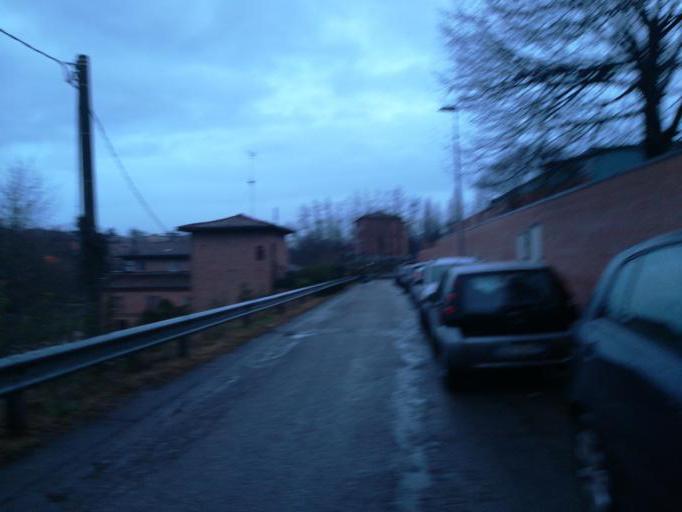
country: IT
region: Emilia-Romagna
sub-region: Provincia di Bologna
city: Progresso
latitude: 44.5484
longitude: 11.3531
